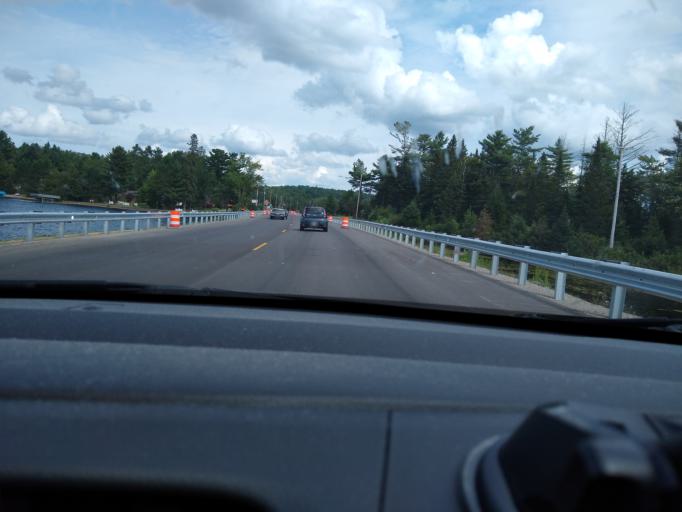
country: US
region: Michigan
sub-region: Baraga County
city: L'Anse
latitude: 46.5531
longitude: -88.2092
